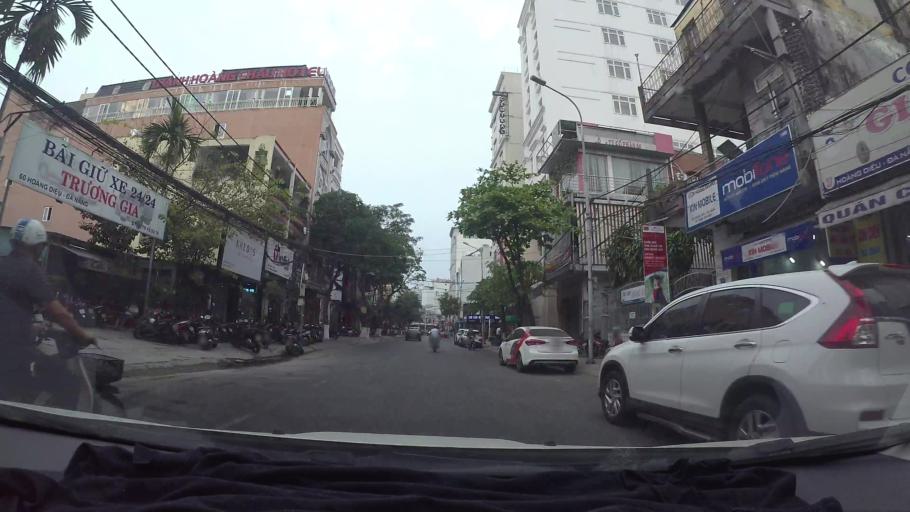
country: VN
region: Da Nang
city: Da Nang
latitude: 16.0649
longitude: 108.2193
